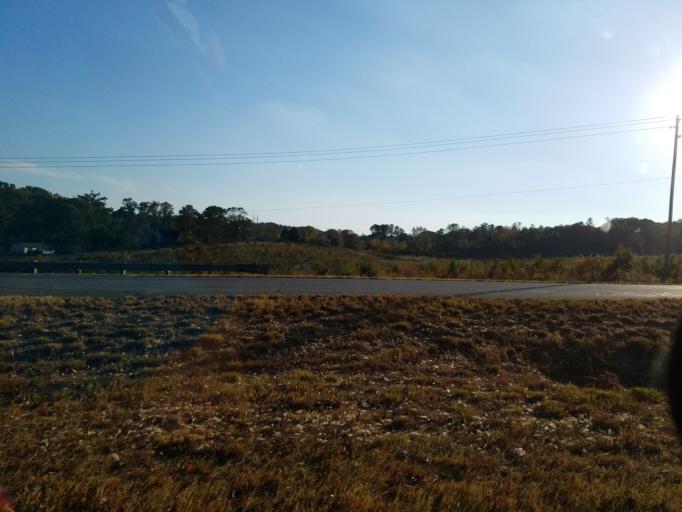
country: US
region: Georgia
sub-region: Bartow County
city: Euharlee
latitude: 34.2230
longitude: -84.8854
